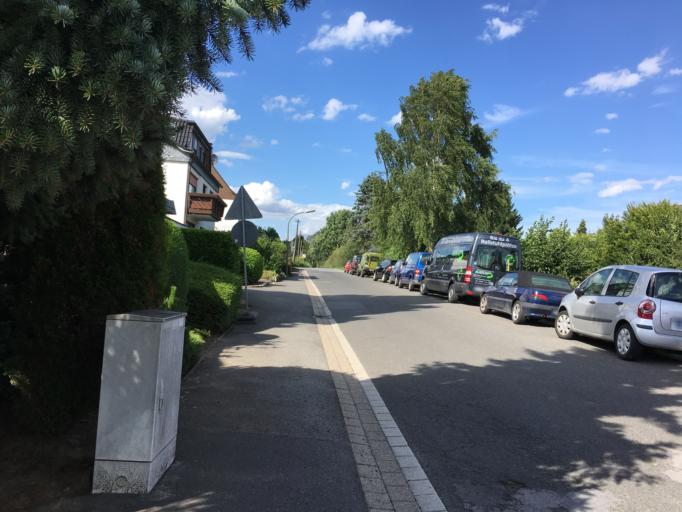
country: DE
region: North Rhine-Westphalia
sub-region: Regierungsbezirk Arnsberg
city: Frondenberg
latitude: 51.4819
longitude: 7.7274
